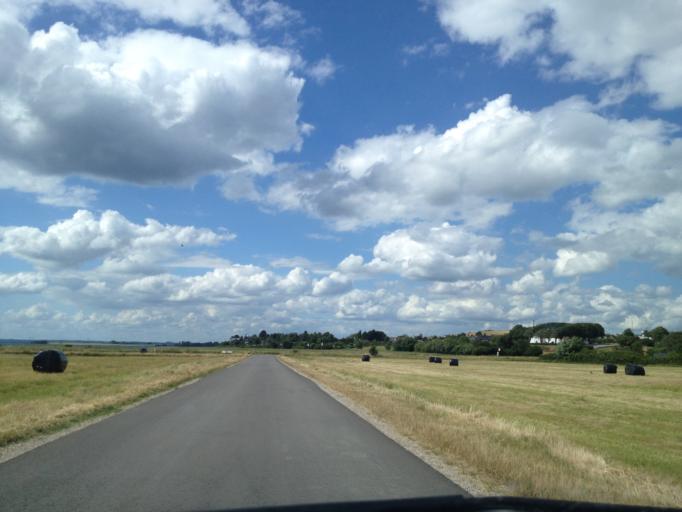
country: DK
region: Central Jutland
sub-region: Syddjurs Kommune
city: Ronde
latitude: 56.2064
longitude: 10.4841
